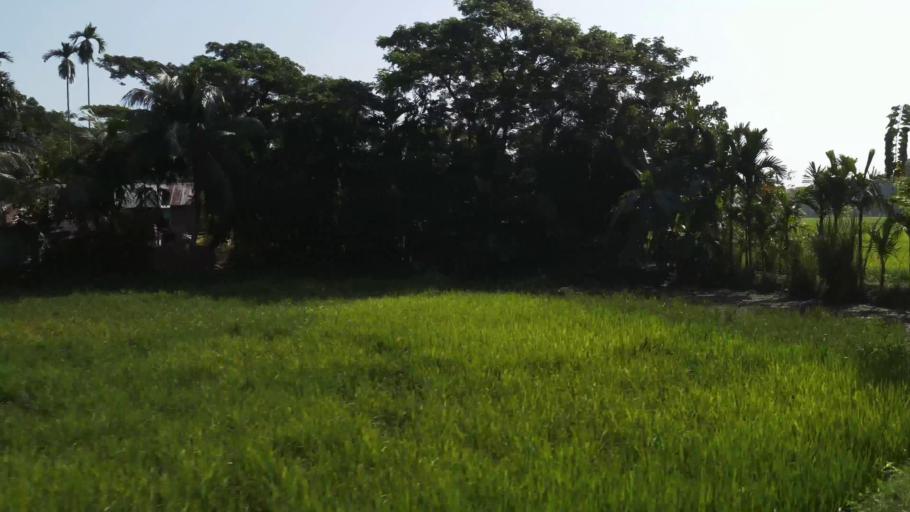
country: BD
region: Dhaka
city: Gafargaon
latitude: 24.5938
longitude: 90.5010
